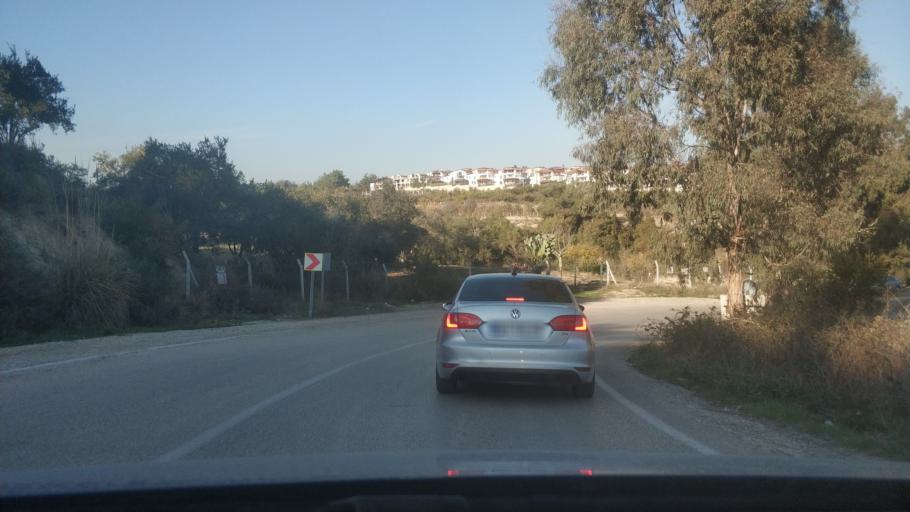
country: TR
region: Adana
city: Adana
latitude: 37.1040
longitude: 35.2945
